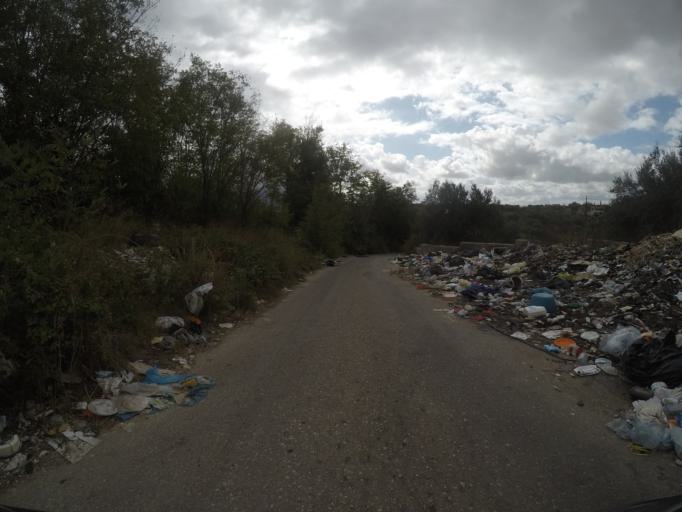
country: IT
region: Sicily
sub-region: Palermo
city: Partinico
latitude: 38.0826
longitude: 13.1088
